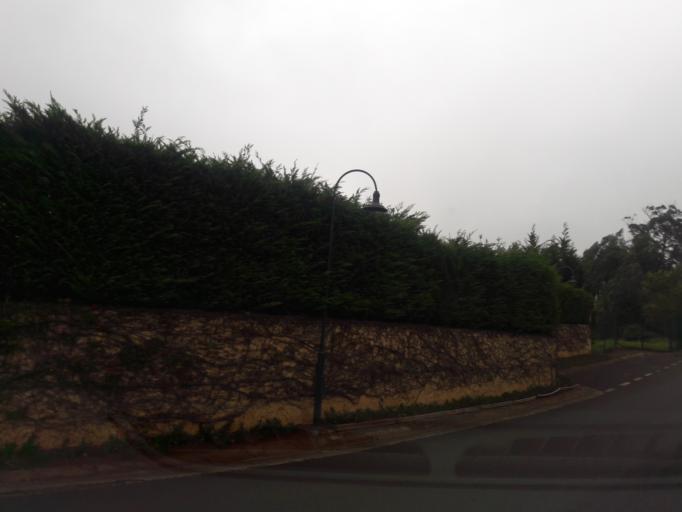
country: PT
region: Madeira
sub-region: Funchal
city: Nossa Senhora do Monte
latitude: 32.6567
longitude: -16.8729
